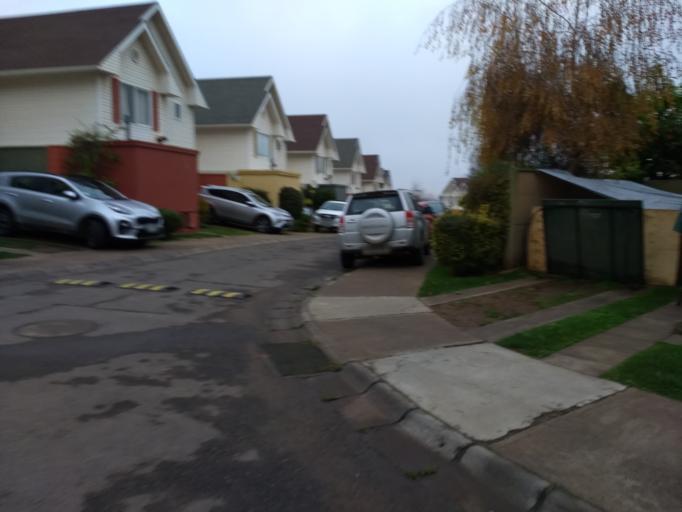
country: CL
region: Valparaiso
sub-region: Provincia de Valparaiso
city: Vina del Mar
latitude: -32.9645
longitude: -71.5183
